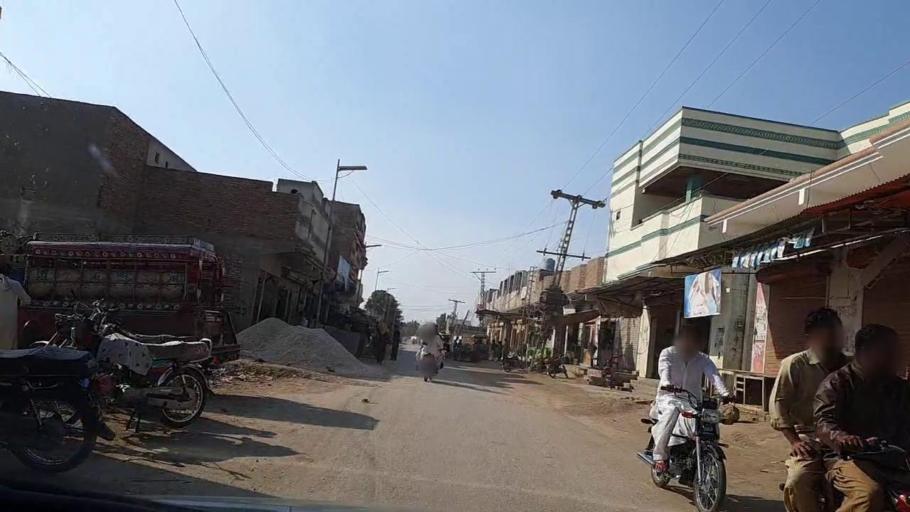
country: PK
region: Sindh
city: Sakrand
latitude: 26.1372
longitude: 68.2672
